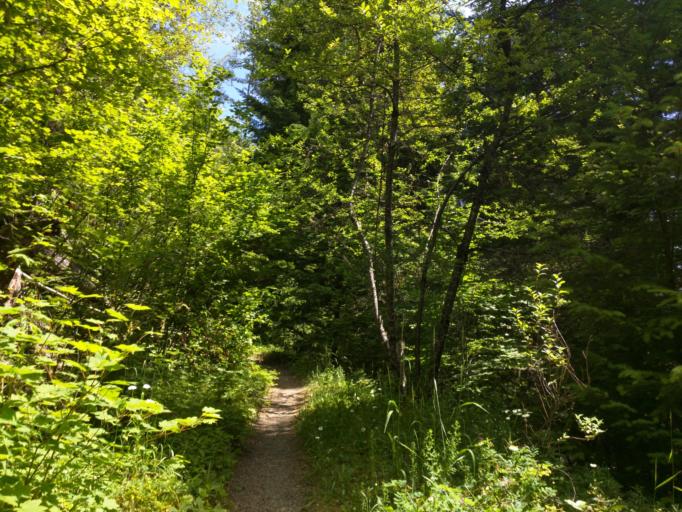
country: CA
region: British Columbia
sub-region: Fraser Valley Regional District
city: Chilliwack
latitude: 48.9139
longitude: -121.8525
